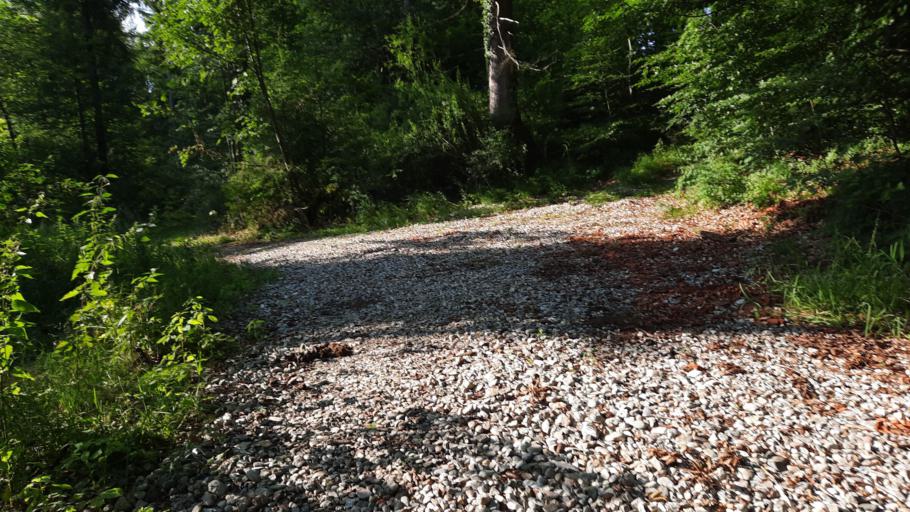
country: DE
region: Bavaria
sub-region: Upper Bavaria
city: Glonn
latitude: 47.9602
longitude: 11.9041
